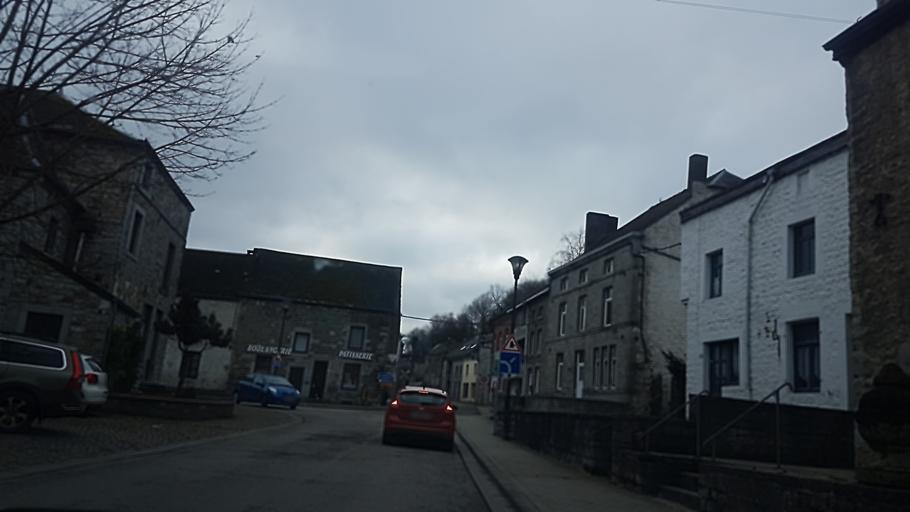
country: BE
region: Wallonia
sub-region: Province de Namur
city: Couvin
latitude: 50.0733
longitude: 4.6074
